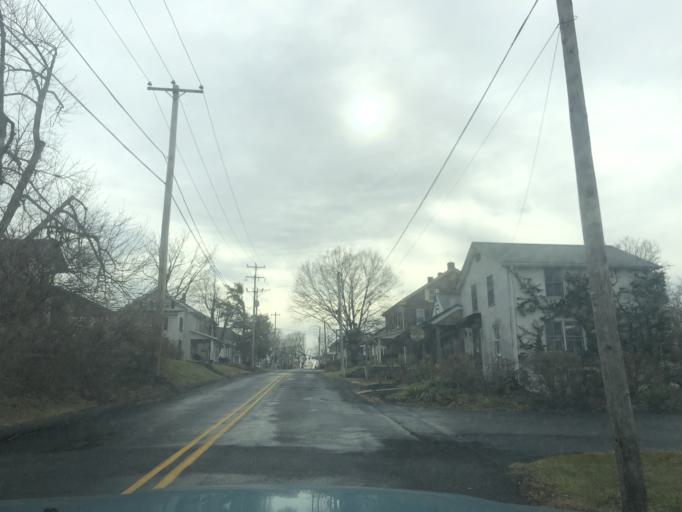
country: US
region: Pennsylvania
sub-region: Montgomery County
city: Harleysville
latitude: 40.2633
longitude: -75.4069
